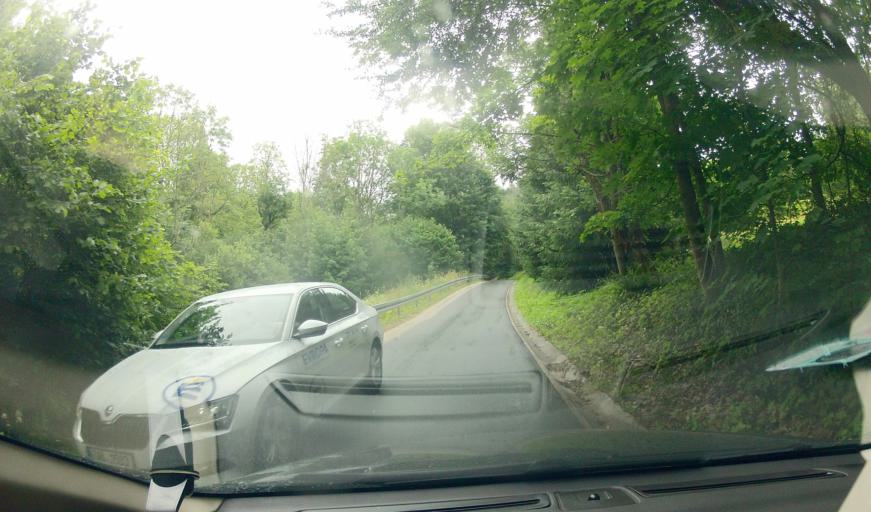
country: PL
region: Lower Silesian Voivodeship
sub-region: Powiat klodzki
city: Miedzylesie
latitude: 50.1187
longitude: 16.6503
